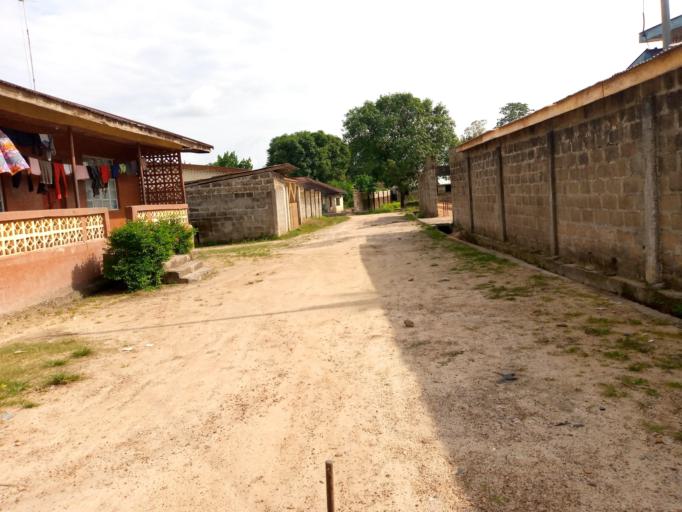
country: SL
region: Northern Province
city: Magburaka
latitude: 8.7246
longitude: -11.9475
